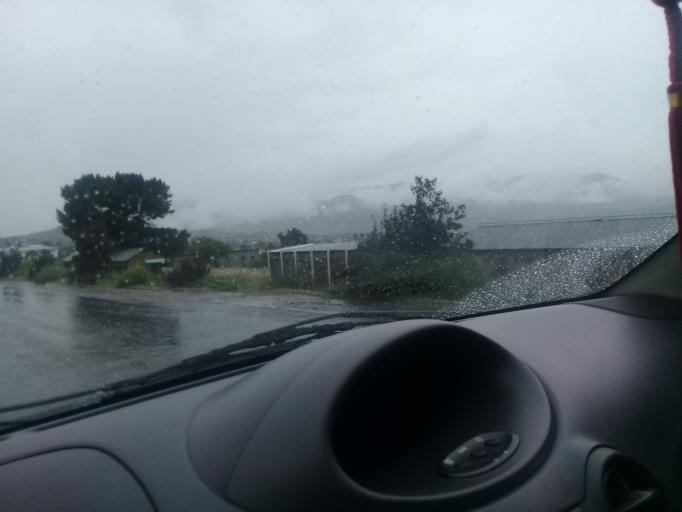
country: LS
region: Mokhotlong
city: Mokhotlong
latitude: -29.2887
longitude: 29.0632
